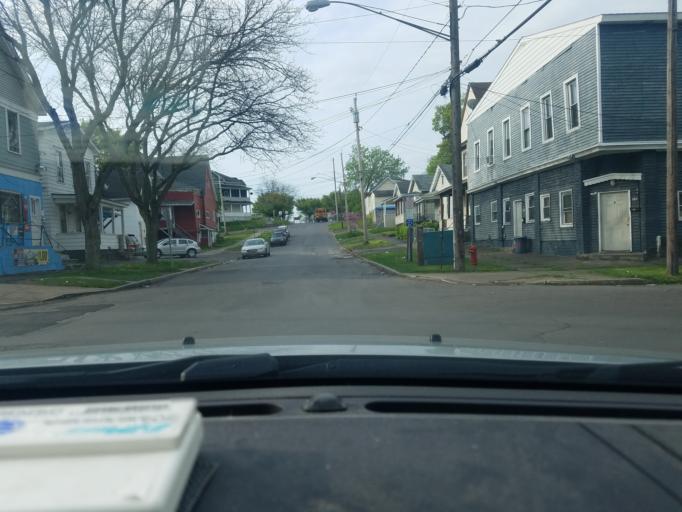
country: US
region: New York
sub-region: Onondaga County
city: Syracuse
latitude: 43.0614
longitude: -76.1414
